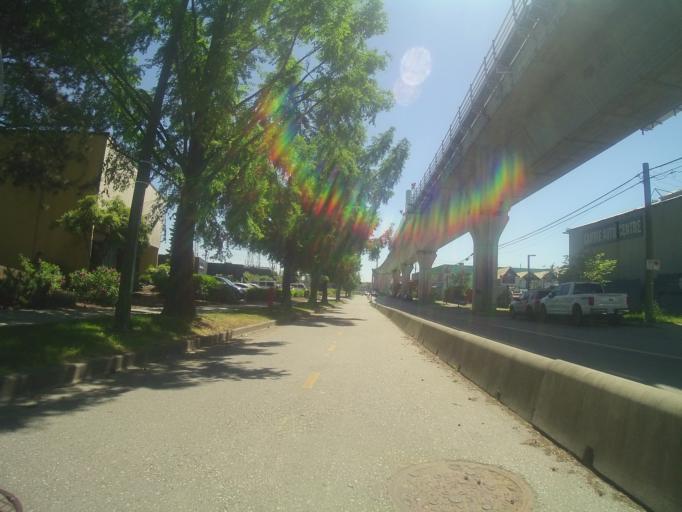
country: CA
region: British Columbia
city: Vancouver
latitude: 49.2075
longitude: -123.1172
